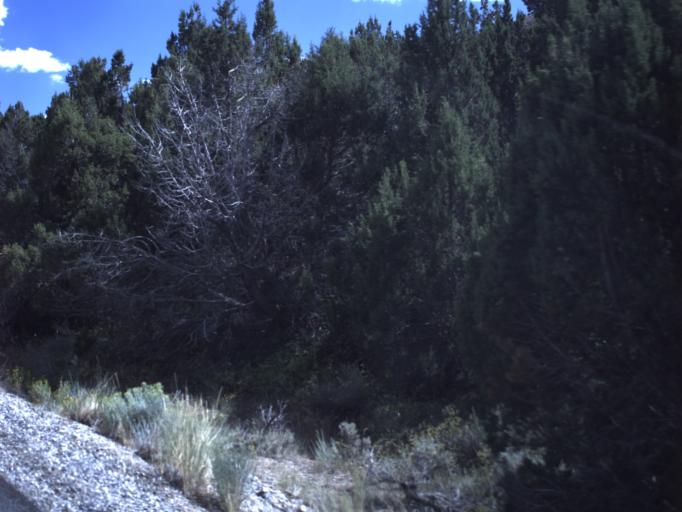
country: US
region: Utah
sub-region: Tooele County
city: Grantsville
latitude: 40.3433
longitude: -112.5820
